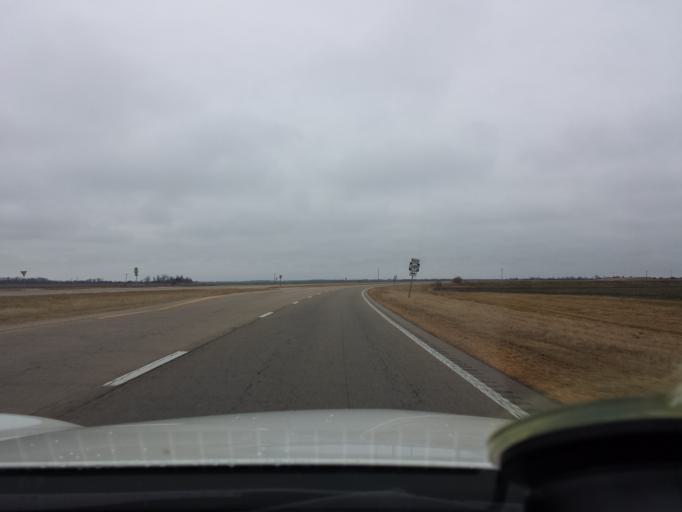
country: US
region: Mississippi
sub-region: Chickasaw County
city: Okolona
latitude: 33.9313
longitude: -88.7382
